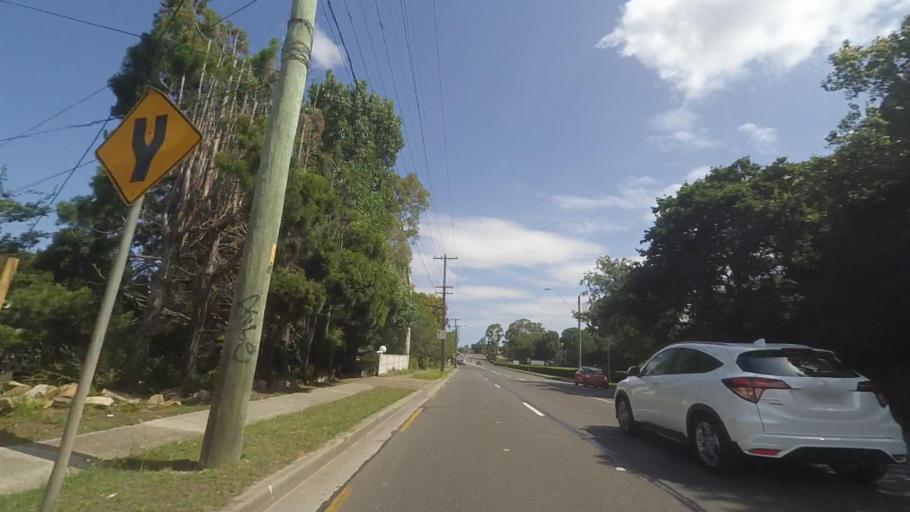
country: AU
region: New South Wales
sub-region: Parramatta
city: Carlingford
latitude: -33.7730
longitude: 151.0512
